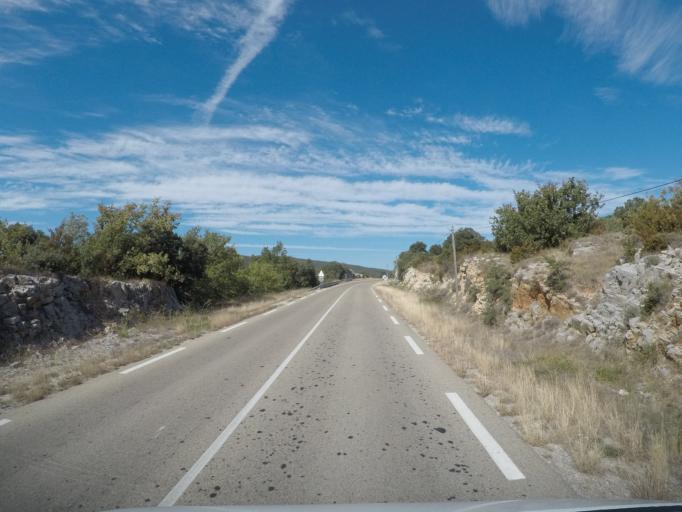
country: FR
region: Languedoc-Roussillon
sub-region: Departement de l'Herault
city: Saint-Martin-de-Londres
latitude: 43.8145
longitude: 3.7436
